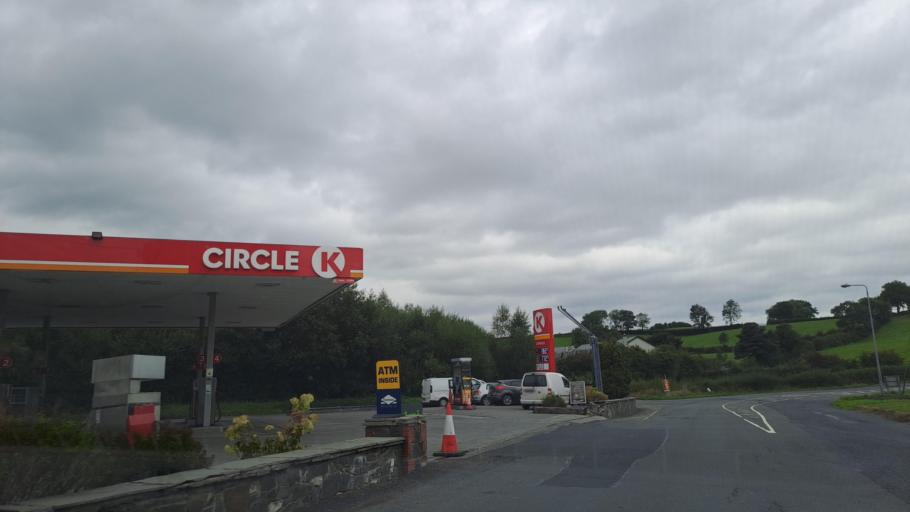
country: IE
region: Ulster
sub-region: An Cabhan
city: Bailieborough
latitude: 53.9975
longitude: -6.8912
